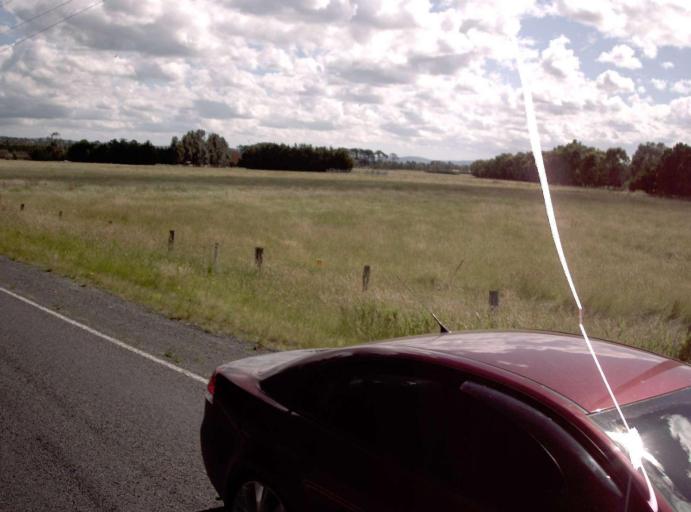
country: AU
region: Victoria
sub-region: Latrobe
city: Morwell
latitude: -38.2898
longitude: 146.4298
